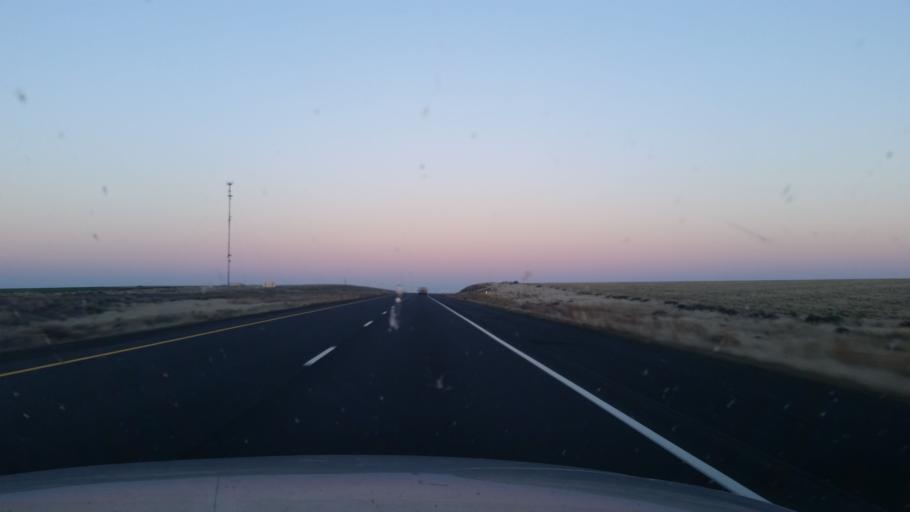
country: US
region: Washington
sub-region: Adams County
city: Ritzville
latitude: 47.0940
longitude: -118.6927
